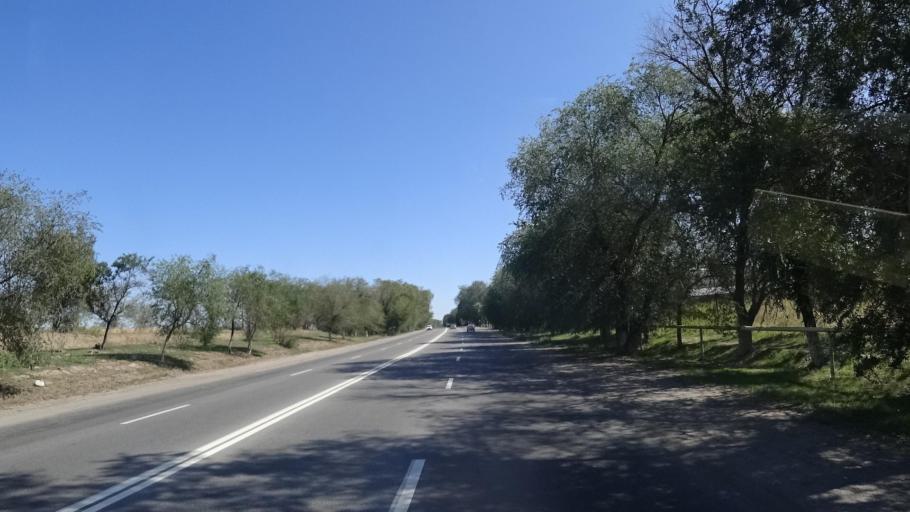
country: KZ
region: Almaty Oblysy
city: Talghar
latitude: 43.4000
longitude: 77.1744
